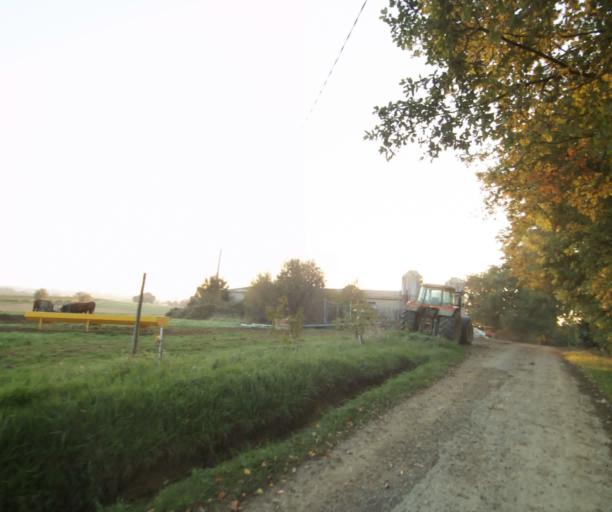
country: FR
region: Midi-Pyrenees
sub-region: Departement du Gers
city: Gondrin
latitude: 43.7901
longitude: 0.2022
